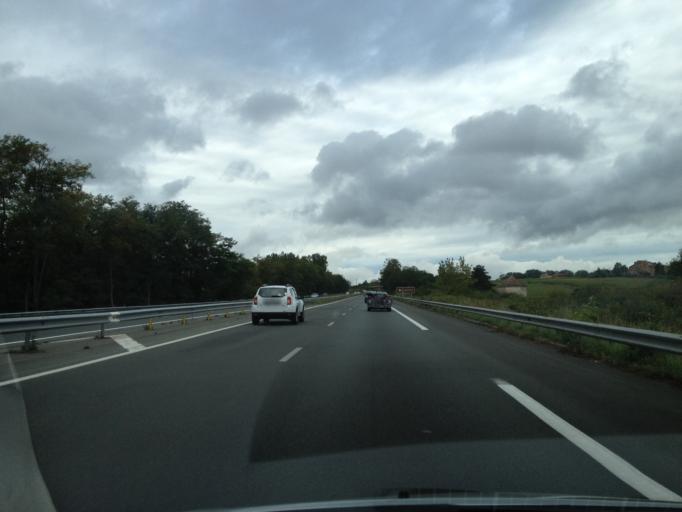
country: FR
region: Aquitaine
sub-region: Departement du Lot-et-Garonne
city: Tonneins
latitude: 44.3776
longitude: 0.2236
